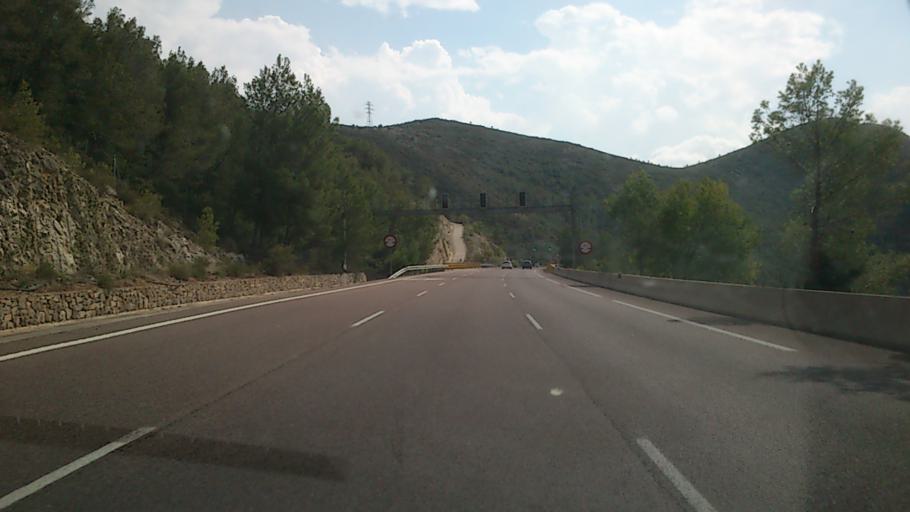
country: ES
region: Valencia
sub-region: Provincia de Valencia
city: L'Olleria
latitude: 38.9316
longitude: -0.5740
